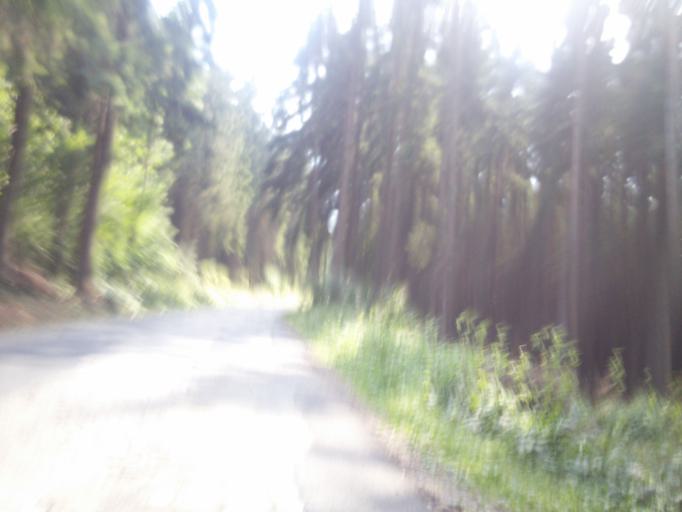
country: CZ
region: South Moravian
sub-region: Okres Blansko
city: Kunstat
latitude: 49.4651
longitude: 16.4561
